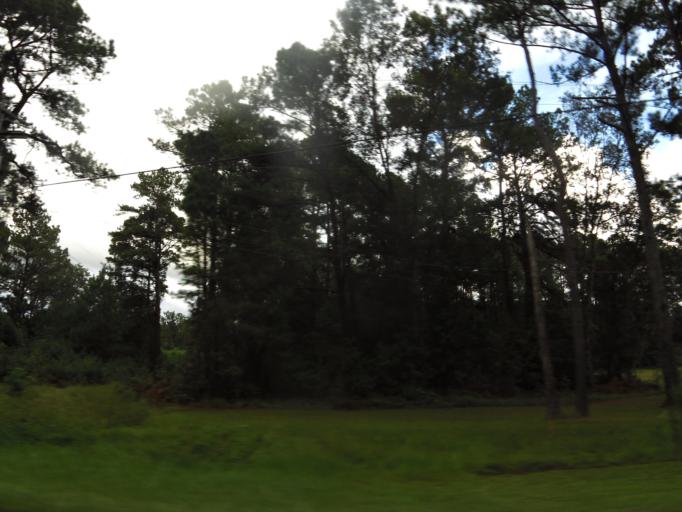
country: US
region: Georgia
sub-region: Liberty County
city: Midway
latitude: 31.8435
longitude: -81.4148
